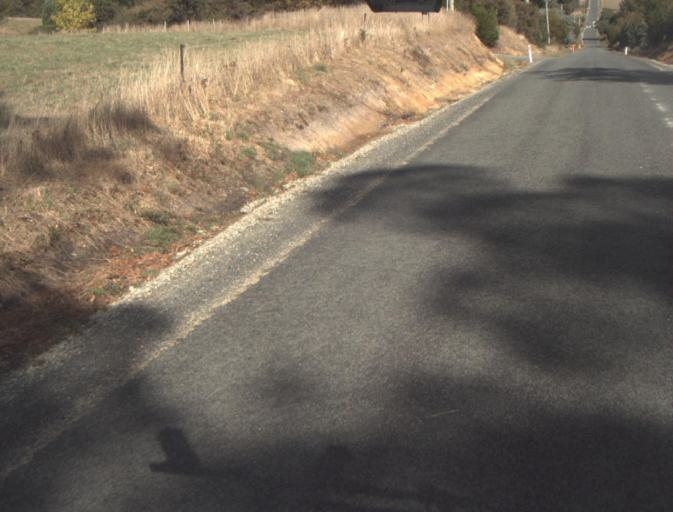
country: AU
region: Tasmania
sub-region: Launceston
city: Mayfield
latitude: -41.2339
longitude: 147.2348
